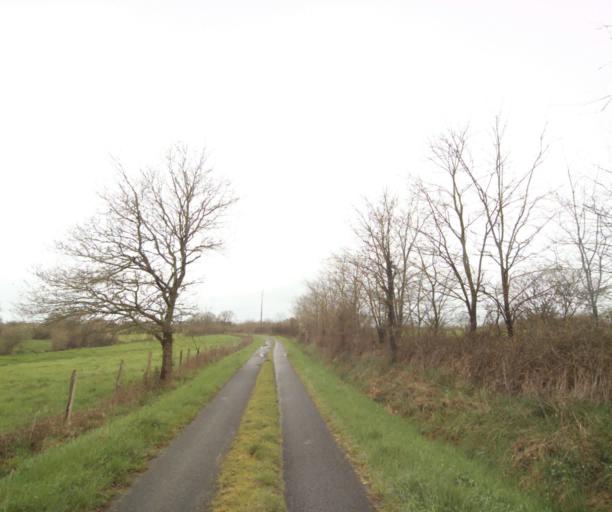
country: FR
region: Pays de la Loire
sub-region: Departement de la Loire-Atlantique
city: Bouvron
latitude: 47.4369
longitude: -1.8722
